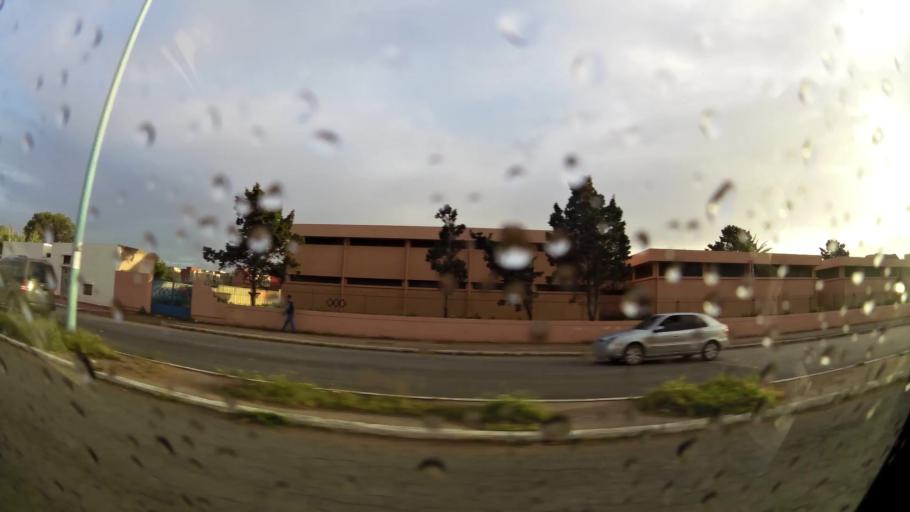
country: MA
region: Doukkala-Abda
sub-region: El-Jadida
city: El Jadida
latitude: 33.2385
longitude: -8.4877
